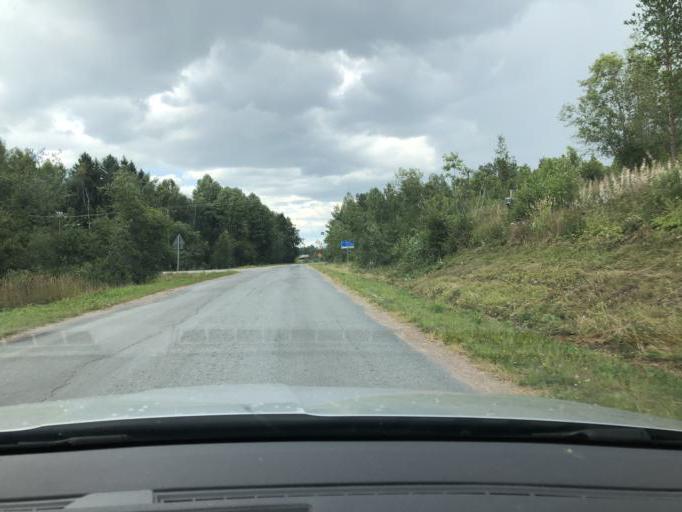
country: SE
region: Vaesternorrland
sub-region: Solleftea Kommun
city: Solleftea
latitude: 63.2130
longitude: 17.1983
